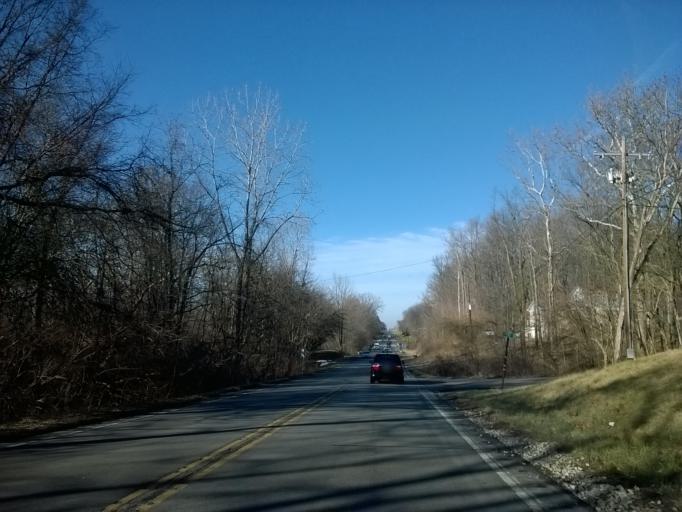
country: US
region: Indiana
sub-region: Boone County
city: Zionsville
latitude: 39.9693
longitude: -86.2506
